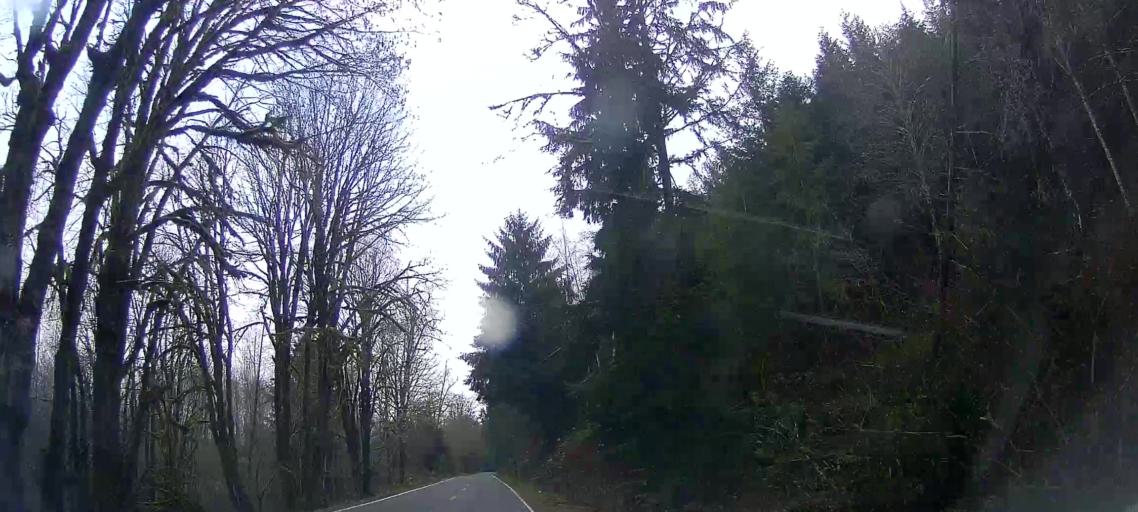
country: US
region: Washington
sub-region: Skagit County
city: Sedro-Woolley
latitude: 48.5125
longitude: -121.9347
